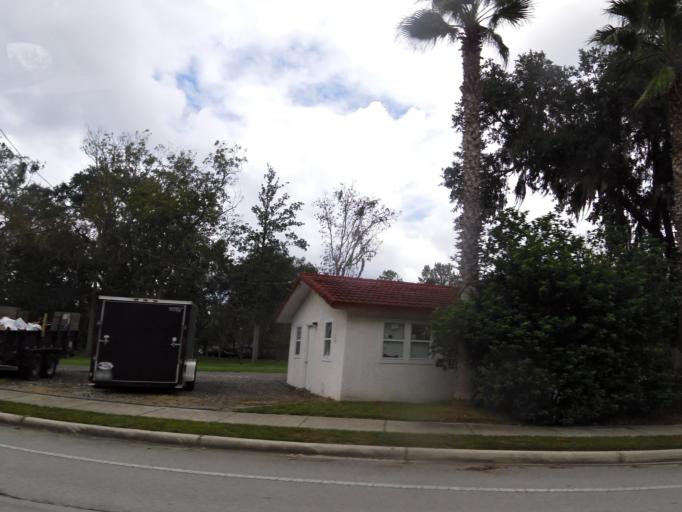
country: US
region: Florida
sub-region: Clay County
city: Lakeside
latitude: 30.0996
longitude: -81.7482
